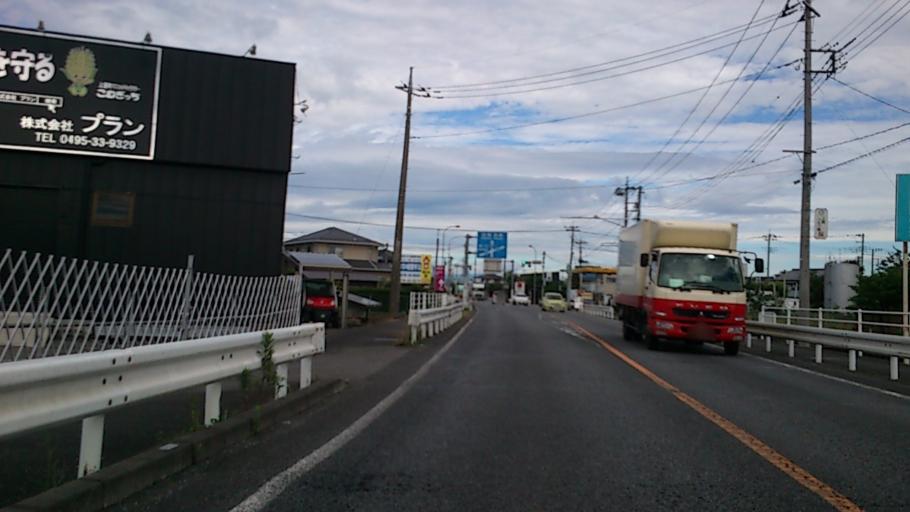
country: JP
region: Saitama
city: Honjo
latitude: 36.2596
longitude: 139.1484
